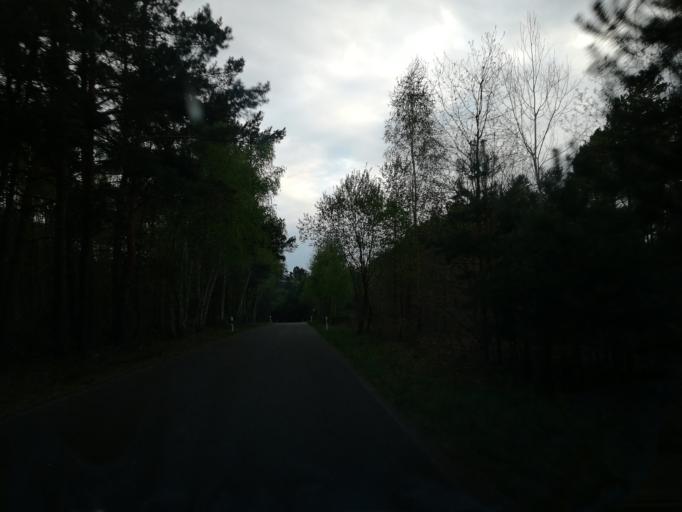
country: DE
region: Brandenburg
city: Calau
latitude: 51.7968
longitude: 13.8841
